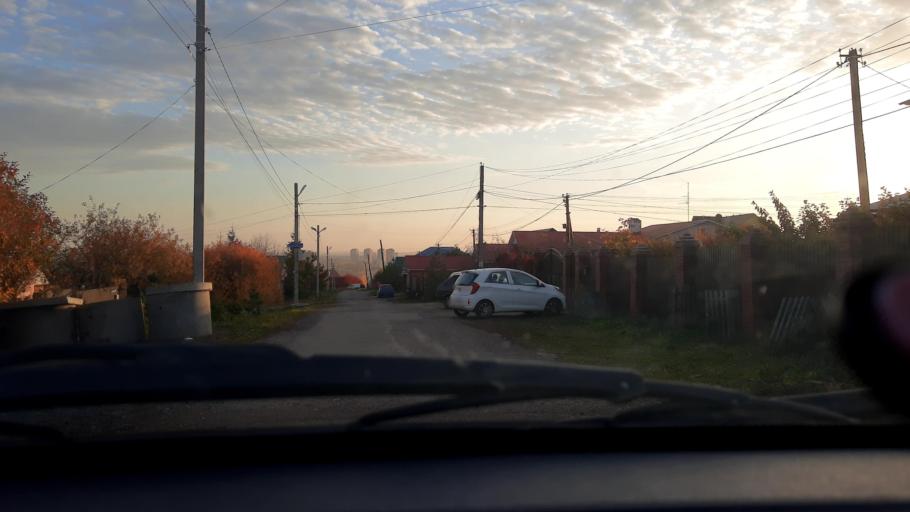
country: RU
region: Bashkortostan
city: Mikhaylovka
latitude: 54.8136
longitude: 55.8892
